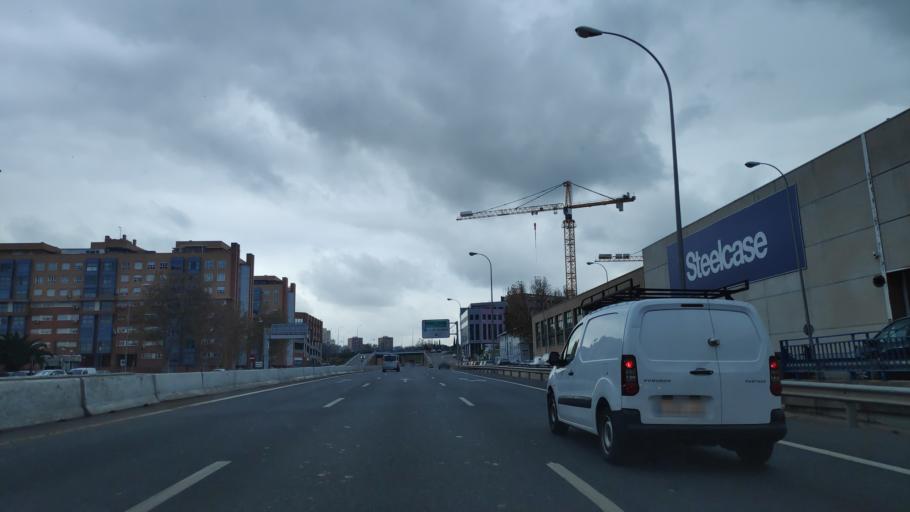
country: ES
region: Madrid
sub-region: Provincia de Madrid
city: Usera
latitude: 40.3794
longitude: -3.6925
